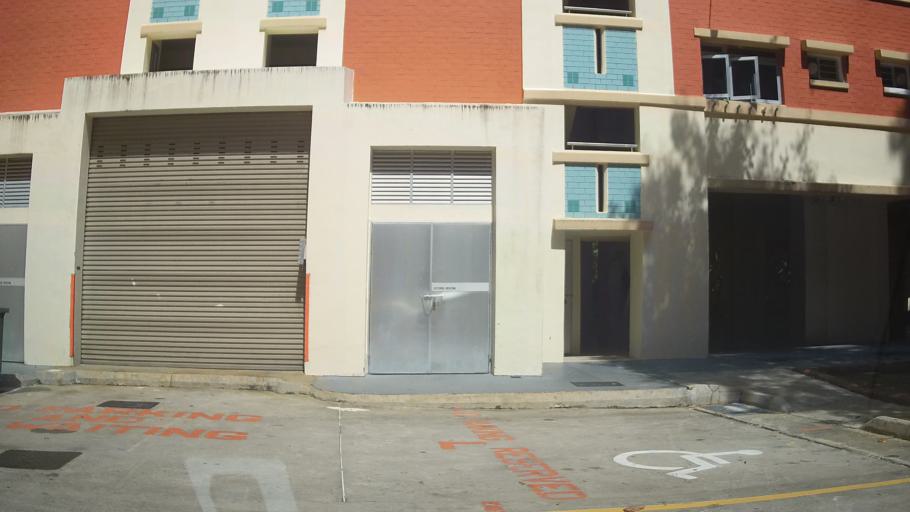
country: MY
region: Johor
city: Kampung Pasir Gudang Baru
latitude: 1.3762
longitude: 103.9446
